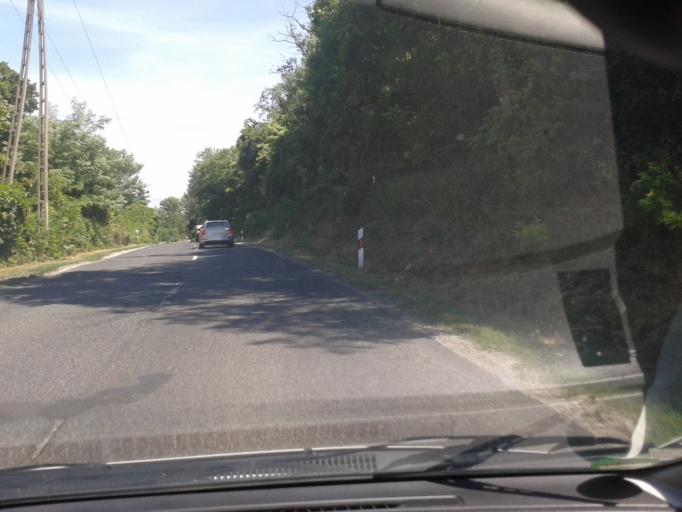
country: HU
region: Pest
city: Szob
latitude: 47.8136
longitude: 18.8158
